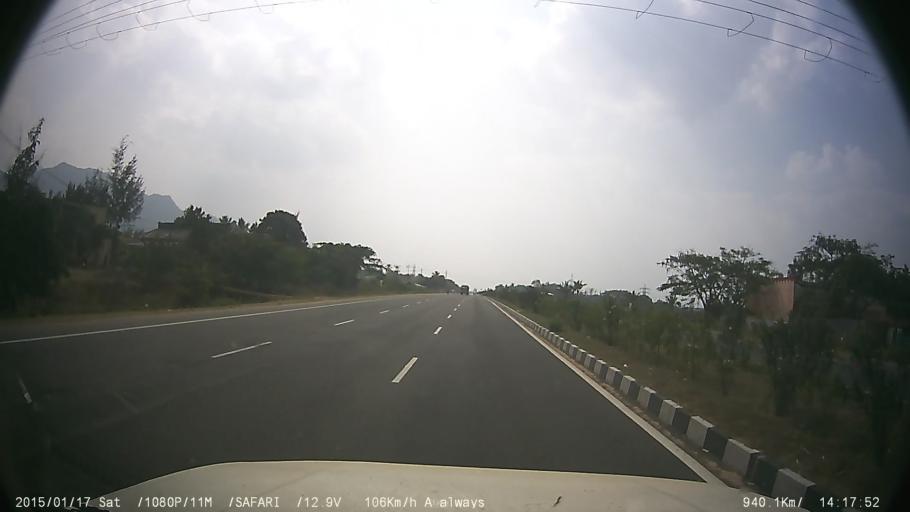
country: IN
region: Tamil Nadu
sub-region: Vellore
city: Ambur
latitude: 12.7358
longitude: 78.6860
